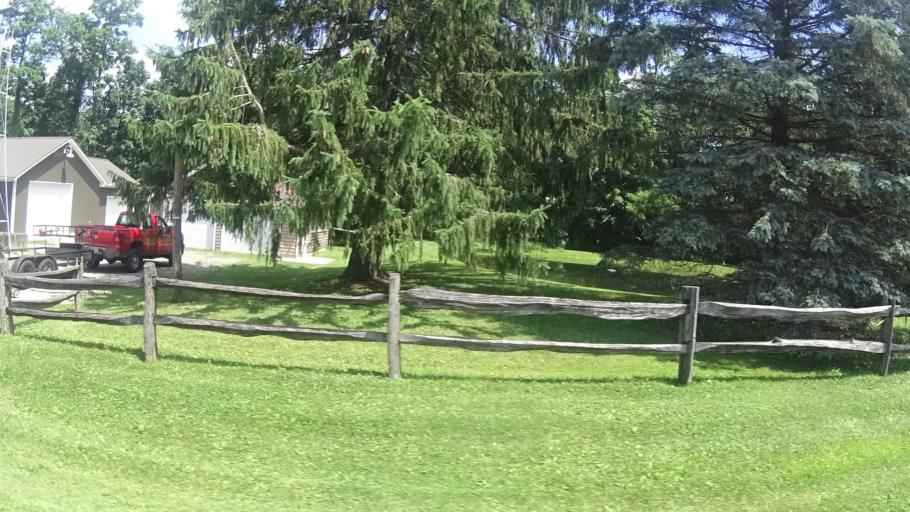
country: US
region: Ohio
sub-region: Huron County
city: Wakeman
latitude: 41.3216
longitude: -82.3589
